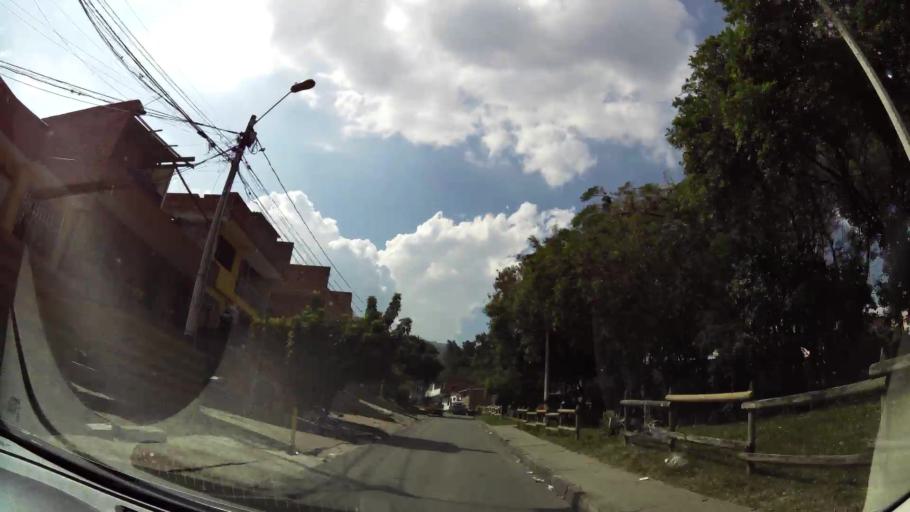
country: CO
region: Antioquia
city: Medellin
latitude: 6.2856
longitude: -75.5763
